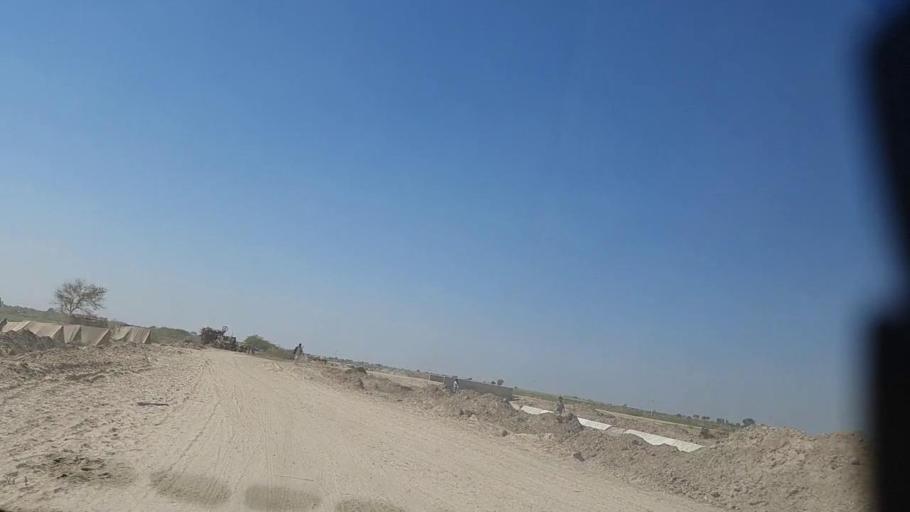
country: PK
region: Sindh
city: Mirwah Gorchani
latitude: 25.2266
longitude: 69.0186
